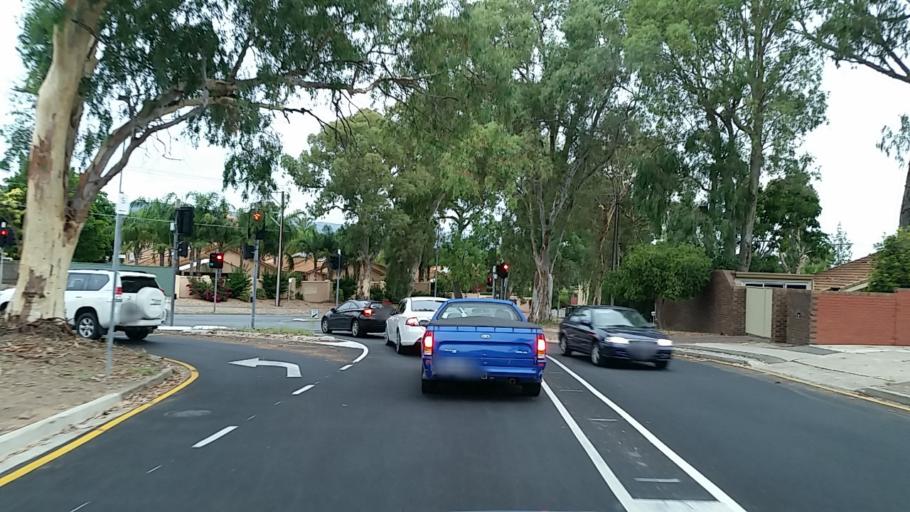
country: AU
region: South Australia
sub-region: Campbelltown
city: Paradise
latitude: -34.8636
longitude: 138.6800
